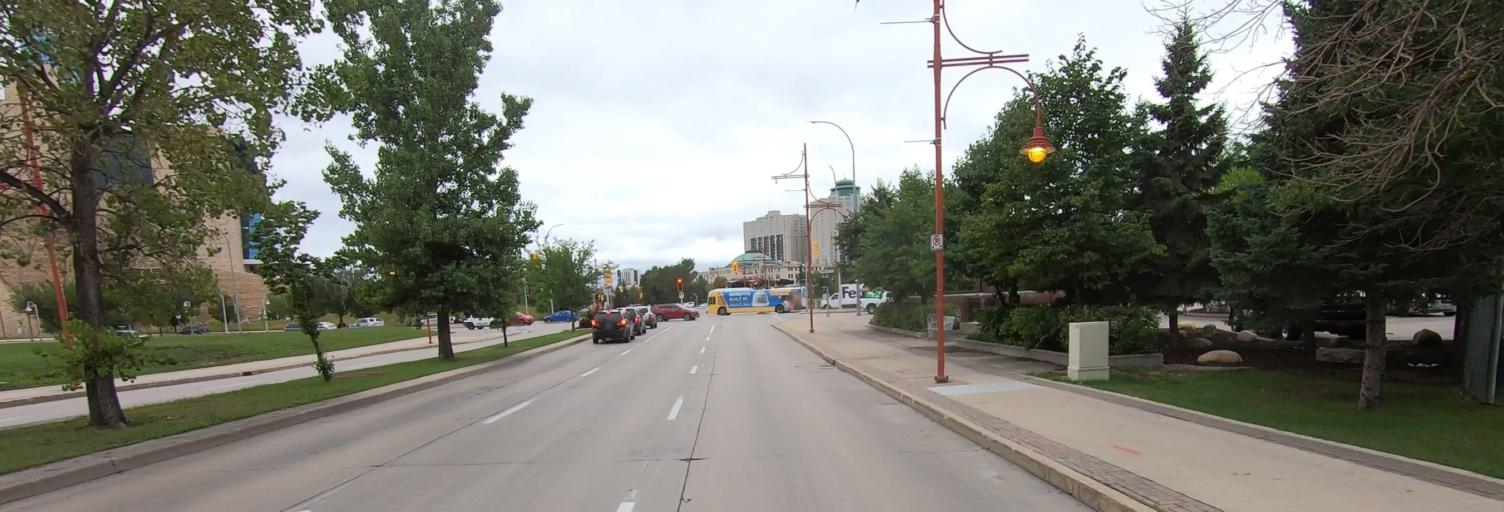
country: CA
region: Manitoba
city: Winnipeg
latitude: 49.8929
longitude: -97.1319
